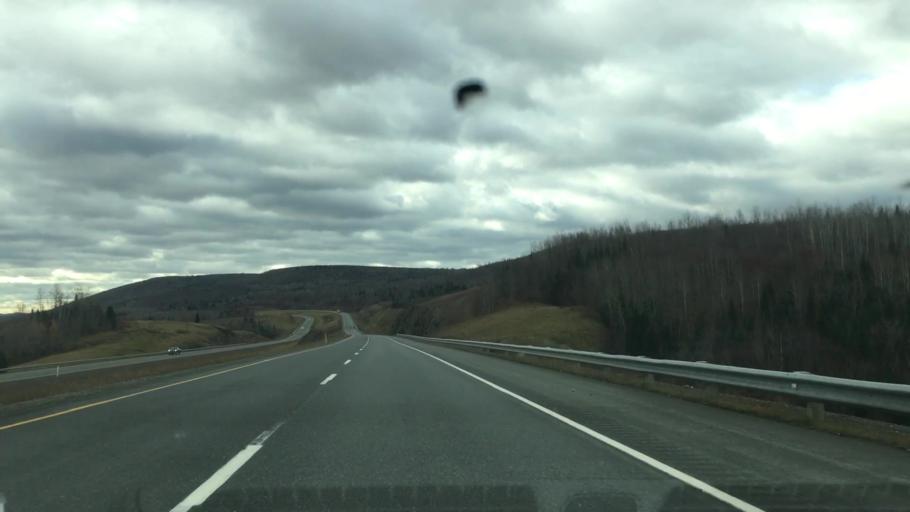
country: US
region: Maine
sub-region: Aroostook County
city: Fort Fairfield
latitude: 46.7117
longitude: -67.7359
